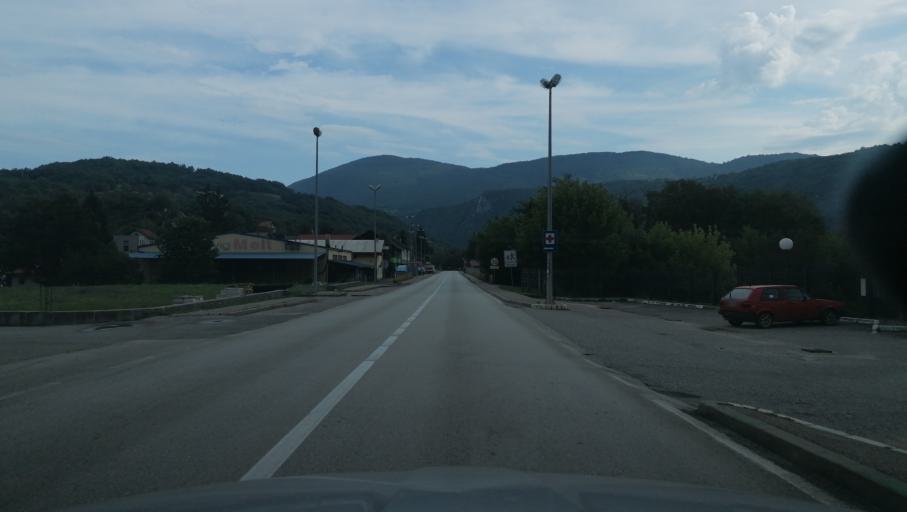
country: BA
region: Republika Srpska
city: Hiseti
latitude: 44.6153
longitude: 17.1432
